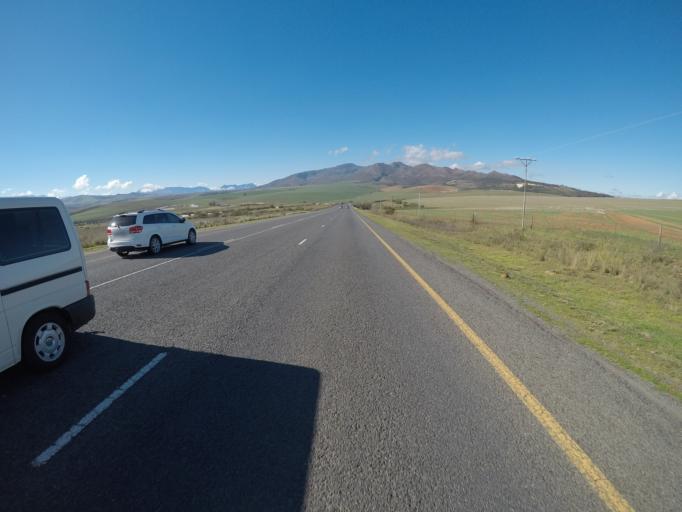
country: ZA
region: Western Cape
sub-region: Overberg District Municipality
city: Caledon
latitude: -34.2093
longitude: 19.3863
